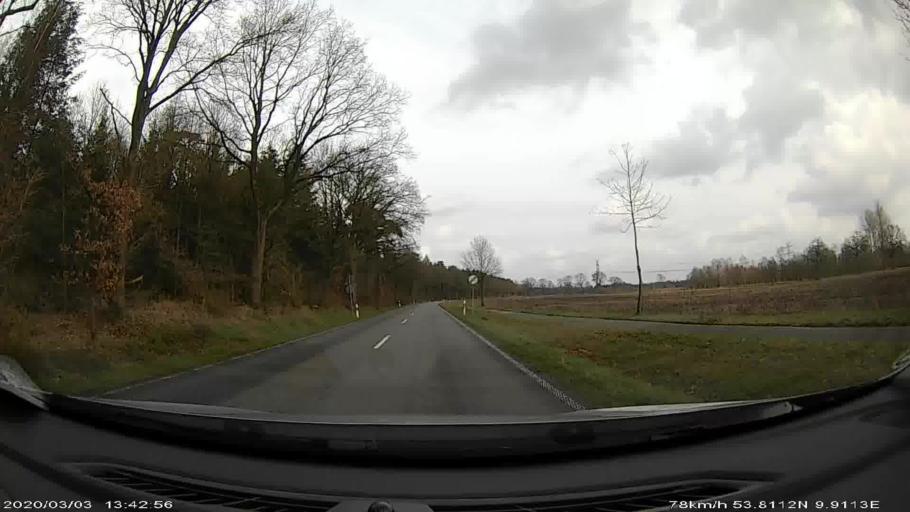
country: DE
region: Schleswig-Holstein
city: Alveslohe
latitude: 53.8121
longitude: 9.9131
